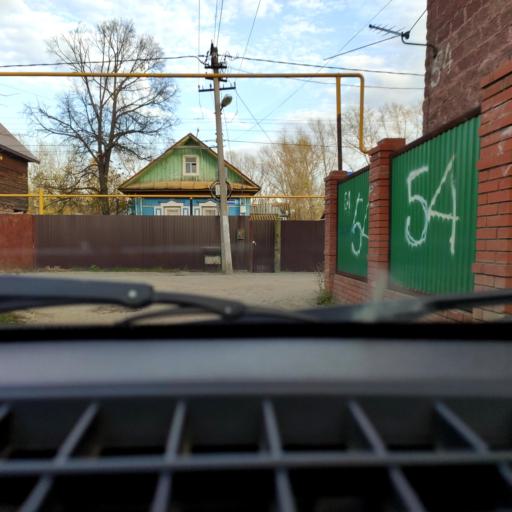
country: RU
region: Bashkortostan
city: Ufa
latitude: 54.6986
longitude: 55.9560
